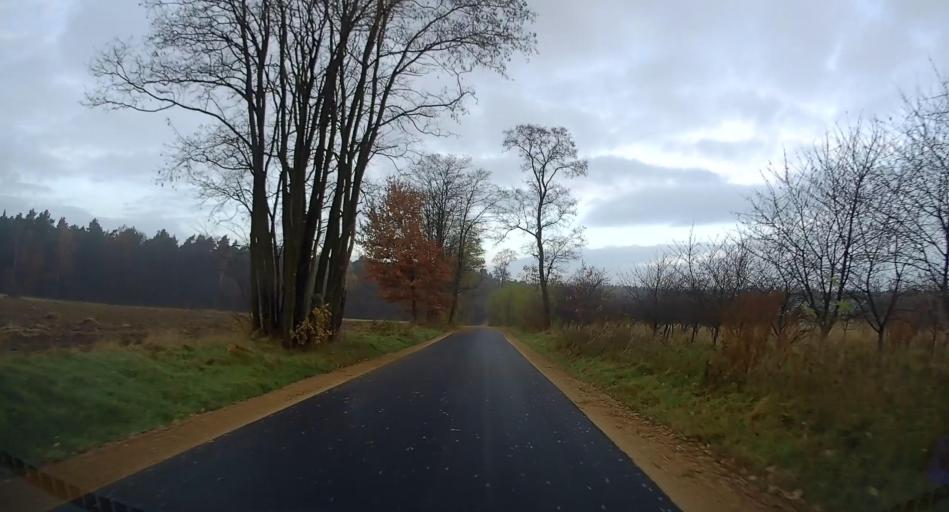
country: PL
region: Lodz Voivodeship
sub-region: Powiat skierniewicki
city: Kowiesy
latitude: 51.9289
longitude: 20.4002
